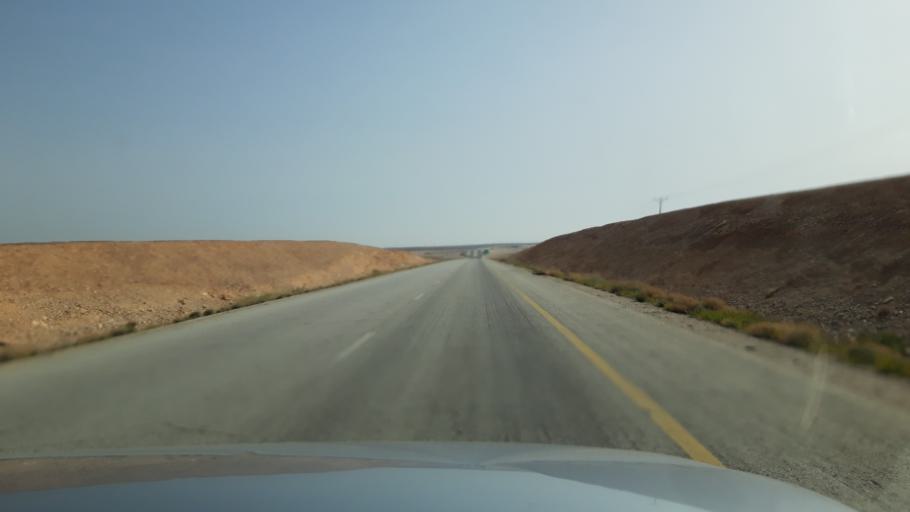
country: JO
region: Amman
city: Al Azraq ash Shamali
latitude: 31.8668
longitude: 36.7166
